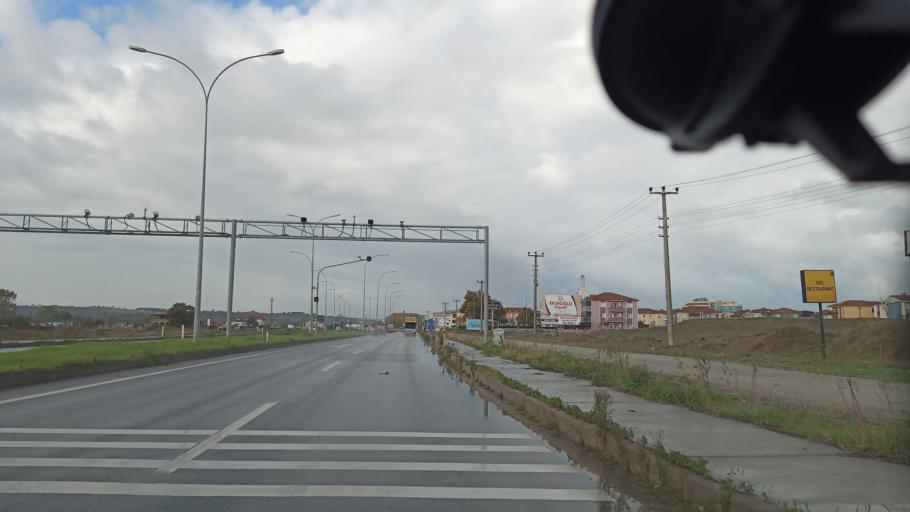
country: TR
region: Sakarya
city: Karasu
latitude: 41.0875
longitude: 30.7436
